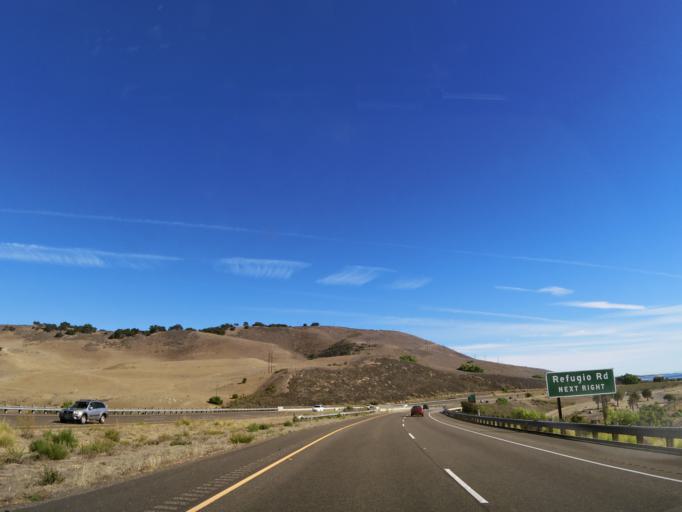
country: US
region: California
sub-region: Santa Barbara County
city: Solvang
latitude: 34.4652
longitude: -120.0714
